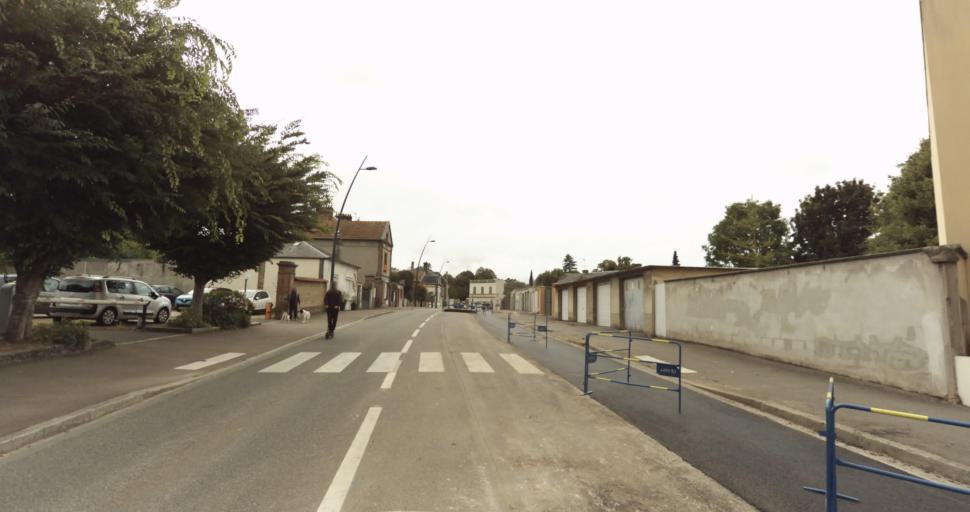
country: FR
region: Haute-Normandie
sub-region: Departement de l'Eure
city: Evreux
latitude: 49.0248
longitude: 1.1556
